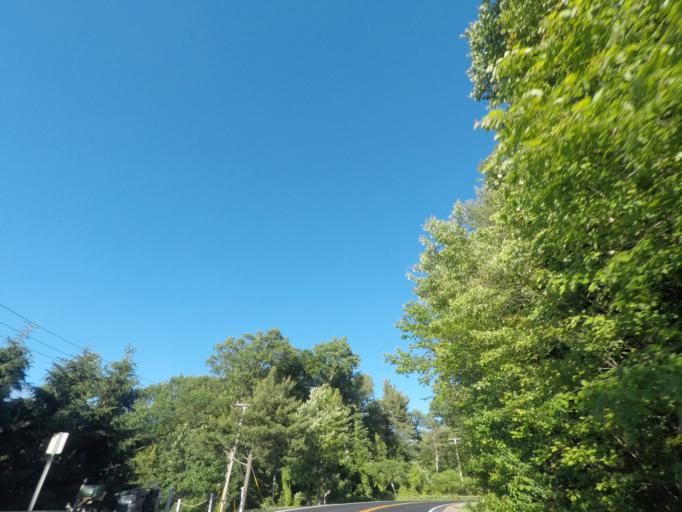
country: US
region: New York
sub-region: Rensselaer County
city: Averill Park
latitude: 42.5862
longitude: -73.5640
